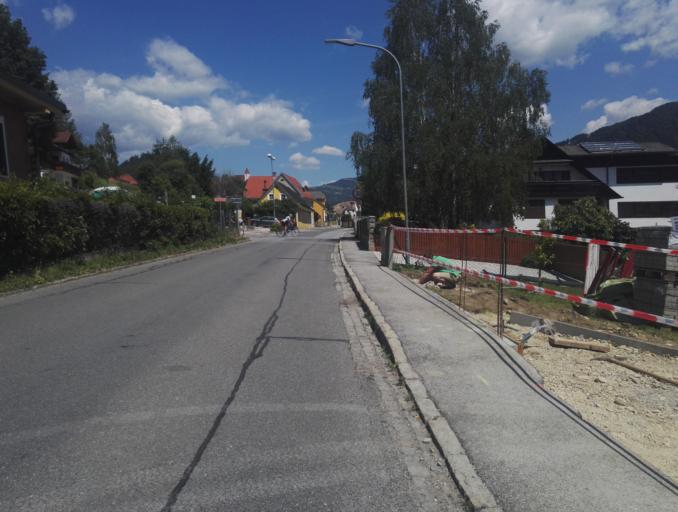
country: AT
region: Styria
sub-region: Politischer Bezirk Graz-Umgebung
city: Deutschfeistritz
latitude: 47.1949
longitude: 15.3357
